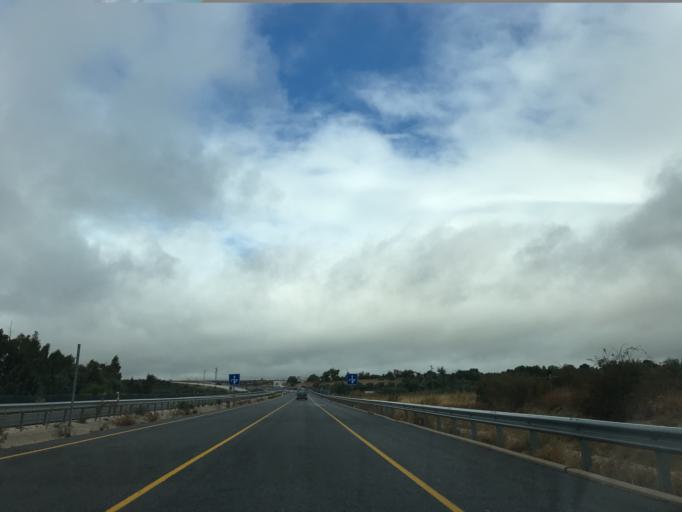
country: ES
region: Andalusia
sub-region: Provincia de Jaen
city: Ubeda
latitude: 38.0203
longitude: -3.4109
